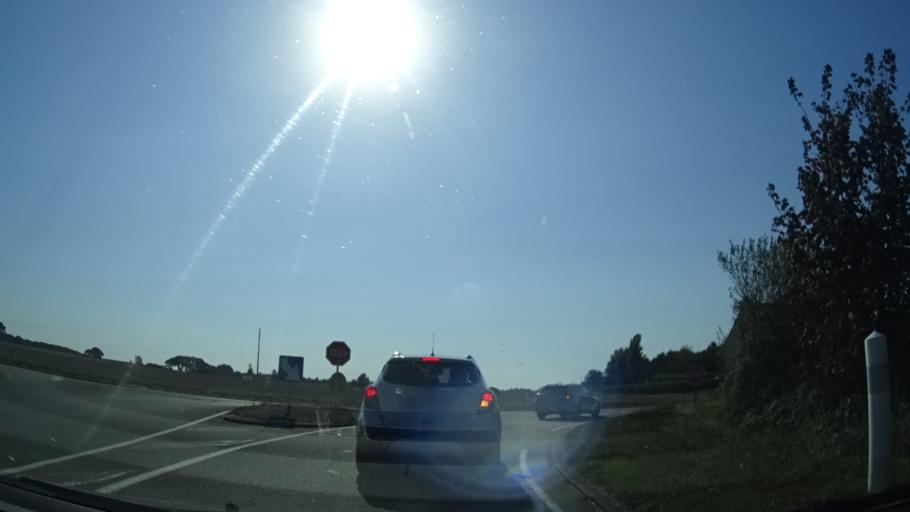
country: FR
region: Brittany
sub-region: Departement du Finistere
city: Plonevez-Porzay
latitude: 48.0939
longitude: -4.2562
